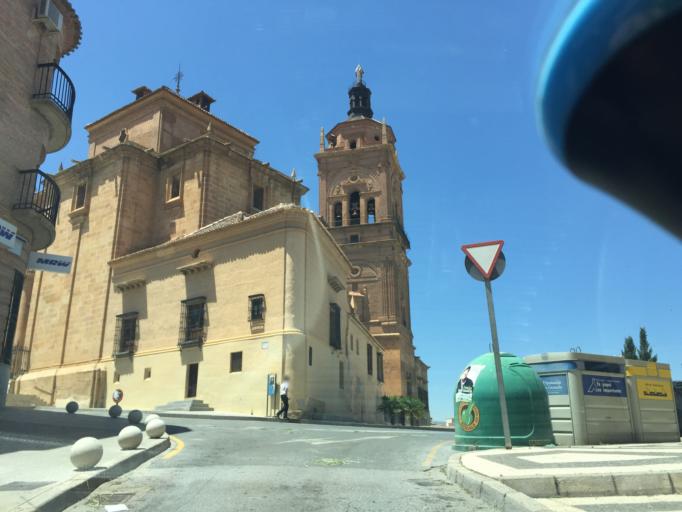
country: ES
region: Andalusia
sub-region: Provincia de Granada
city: Guadix
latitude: 37.3011
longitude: -3.1353
